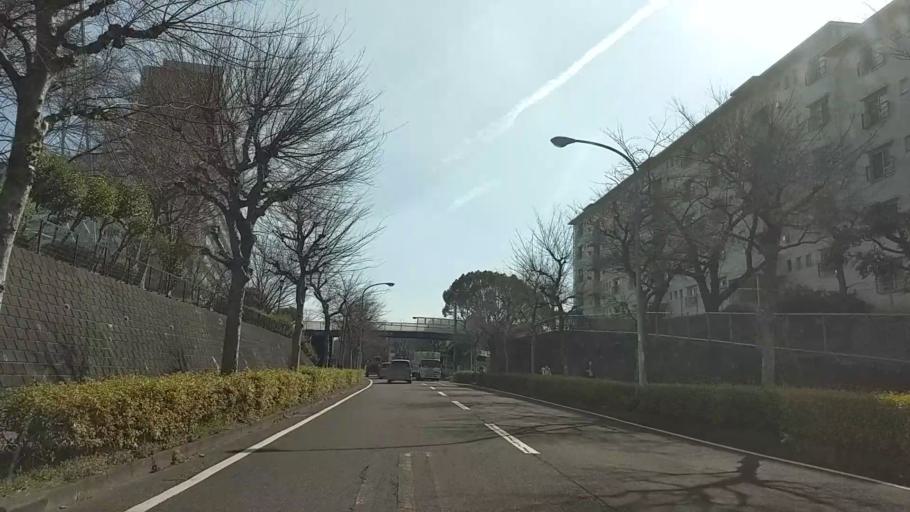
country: JP
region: Kanagawa
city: Kamakura
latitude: 35.3735
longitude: 139.5833
